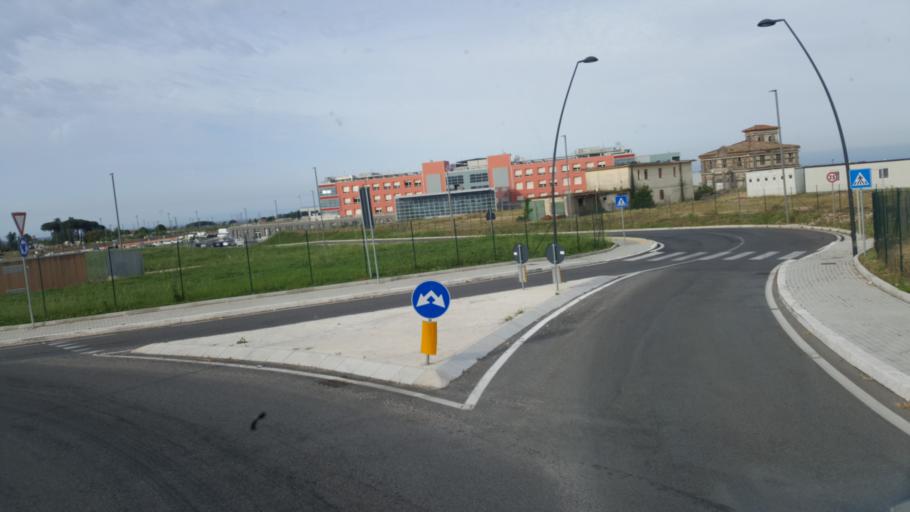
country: IT
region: Latium
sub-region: Citta metropolitana di Roma Capitale
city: Cecchina
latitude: 41.6789
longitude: 12.6508
